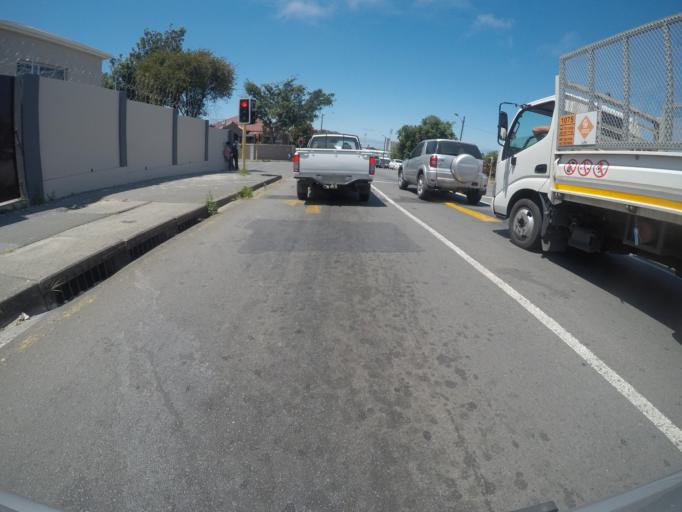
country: ZA
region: Eastern Cape
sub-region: Buffalo City Metropolitan Municipality
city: East London
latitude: -33.0033
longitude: 27.9065
